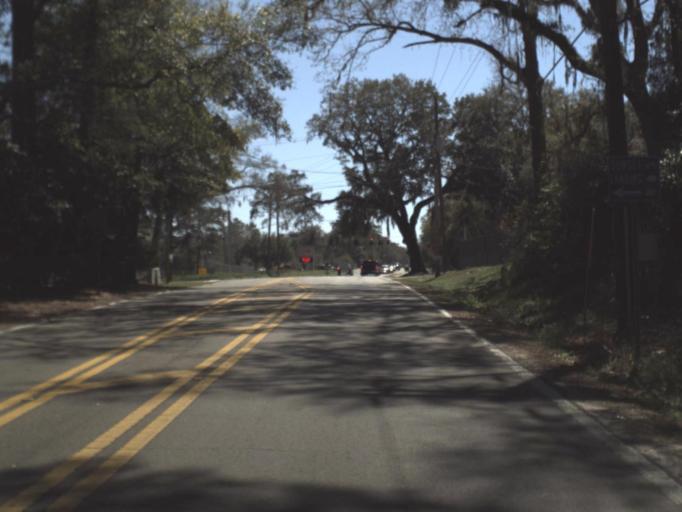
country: US
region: Florida
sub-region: Gadsden County
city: Midway
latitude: 30.5338
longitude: -84.3617
